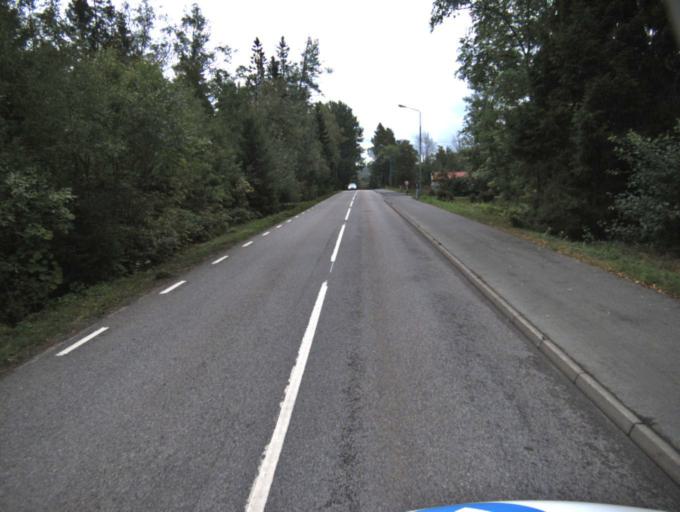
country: SE
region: Vaestra Goetaland
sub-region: Ulricehamns Kommun
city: Ulricehamn
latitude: 57.7726
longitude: 13.4374
